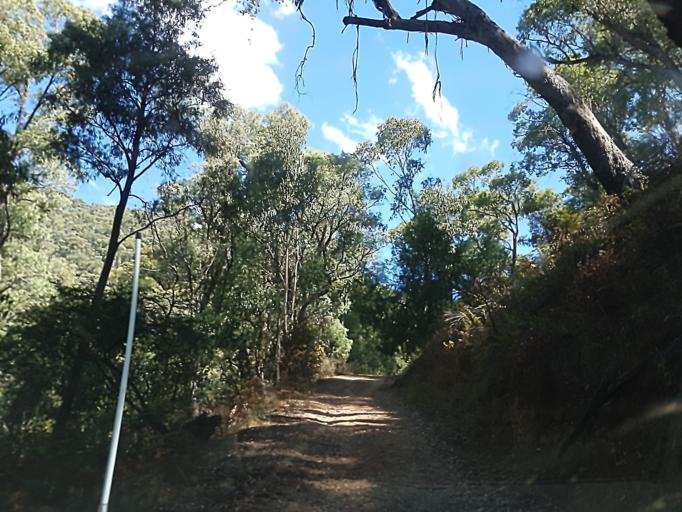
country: AU
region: Victoria
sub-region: Alpine
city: Mount Beauty
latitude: -36.8828
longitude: 147.0378
